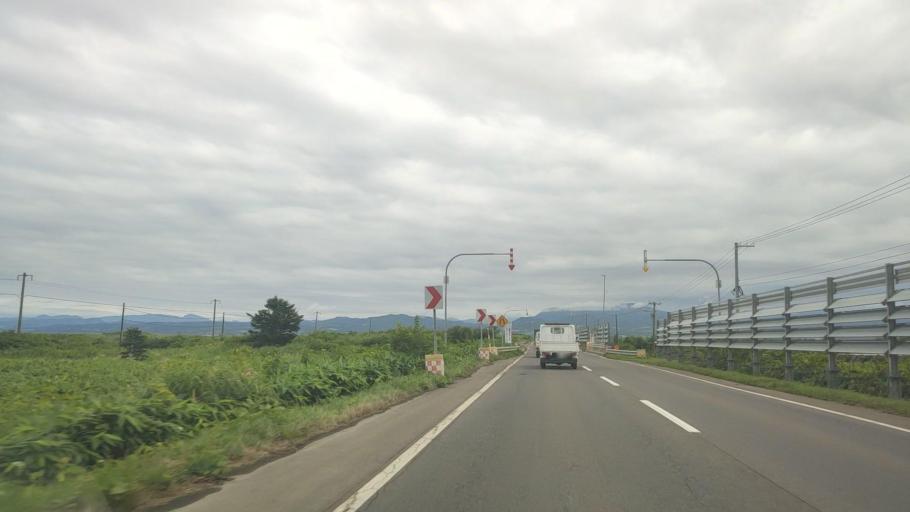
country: JP
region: Hokkaido
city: Nanae
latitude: 42.3043
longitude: 140.2722
